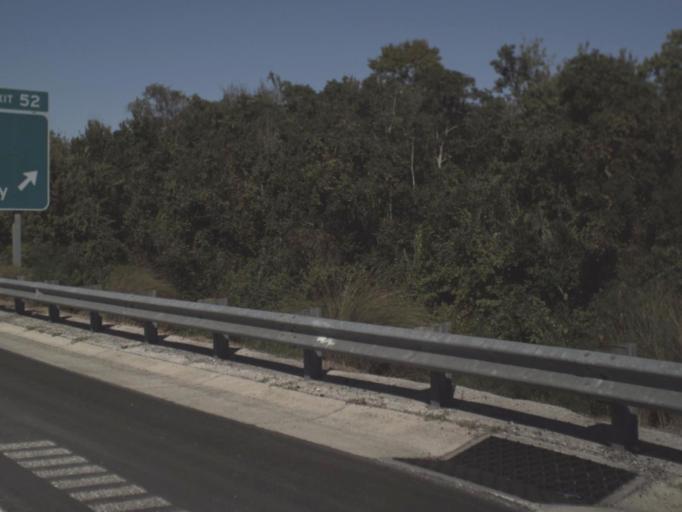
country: US
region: Florida
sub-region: Seminole County
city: Lake Mary
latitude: 28.7811
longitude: -81.2998
